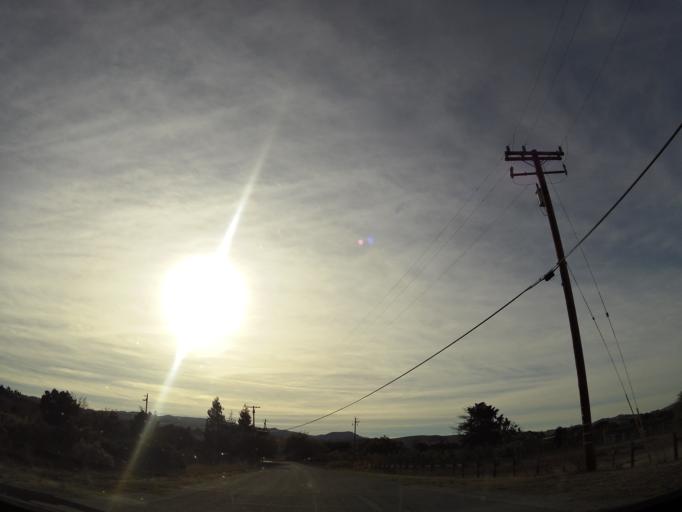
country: US
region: California
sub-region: San Benito County
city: Hollister
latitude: 36.8254
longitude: -121.4045
